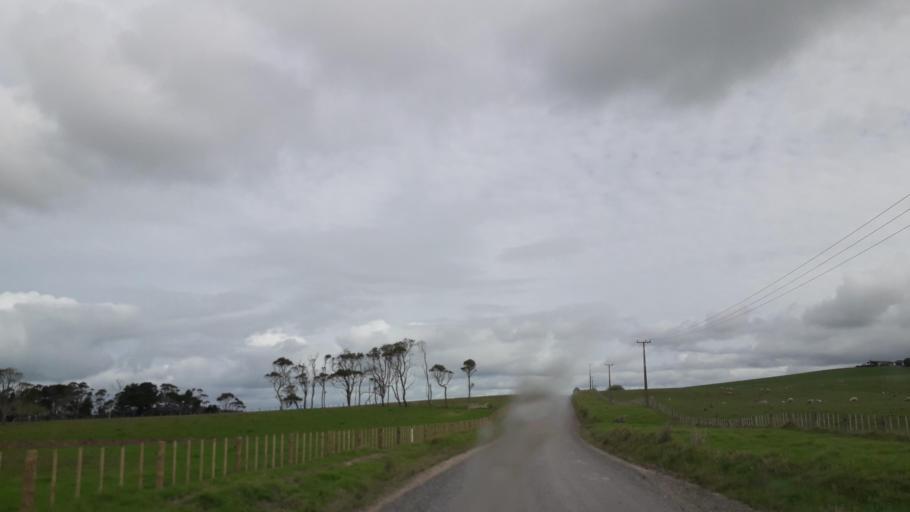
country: NZ
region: Northland
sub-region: Far North District
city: Kerikeri
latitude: -35.1405
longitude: 174.0367
